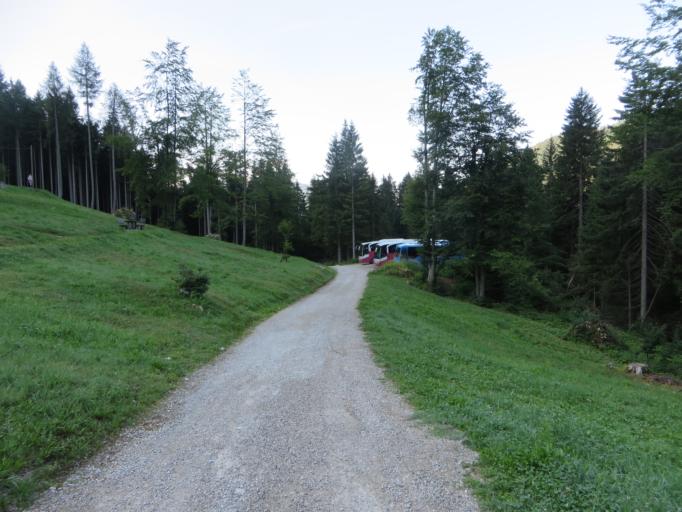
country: IT
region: Trentino-Alto Adige
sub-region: Provincia di Trento
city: Carisolo
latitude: 46.2203
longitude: 10.8281
